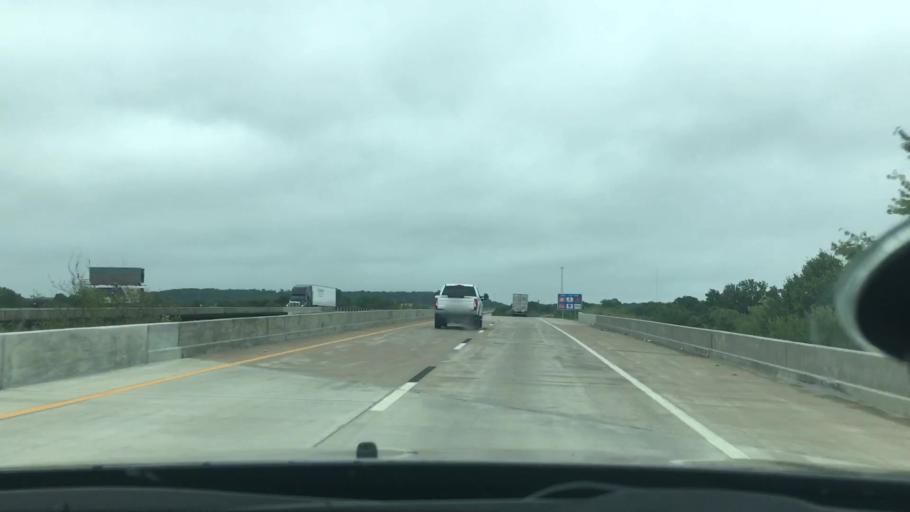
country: US
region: Oklahoma
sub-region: Okmulgee County
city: Henryetta
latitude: 35.4329
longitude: -95.9912
